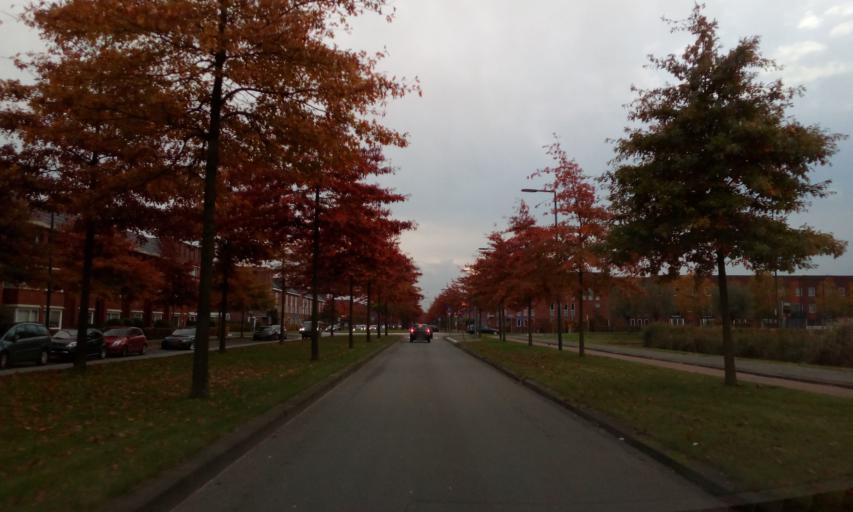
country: NL
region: South Holland
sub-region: Gemeente Capelle aan den IJssel
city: Capelle aan den IJssel
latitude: 51.9761
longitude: 4.5895
